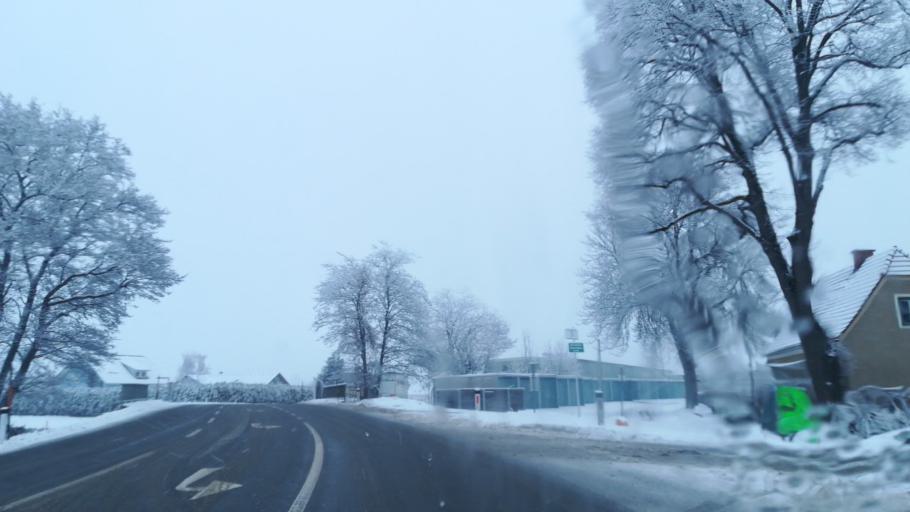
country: AT
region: Styria
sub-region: Politischer Bezirk Murtal
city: Knittelfeld
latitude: 47.2182
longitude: 14.8108
